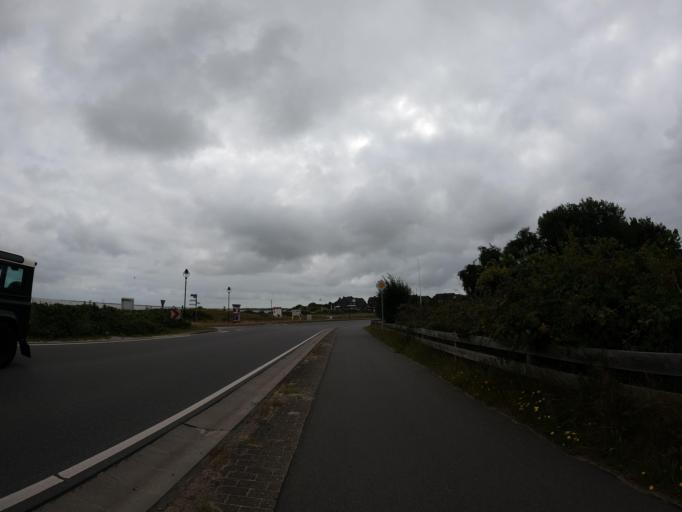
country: DE
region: Schleswig-Holstein
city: Keitum
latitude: 54.9198
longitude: 8.3600
